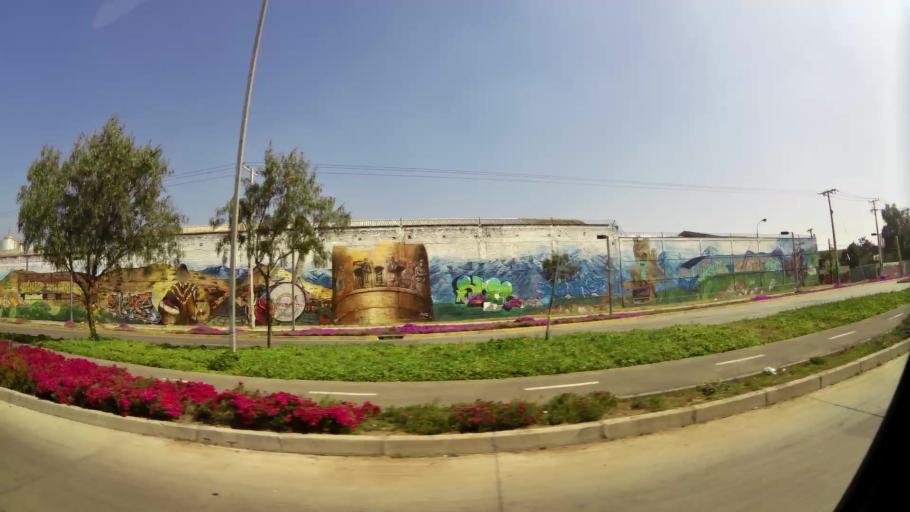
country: CL
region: Santiago Metropolitan
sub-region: Provincia de Santiago
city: Lo Prado
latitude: -33.4241
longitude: -70.6828
